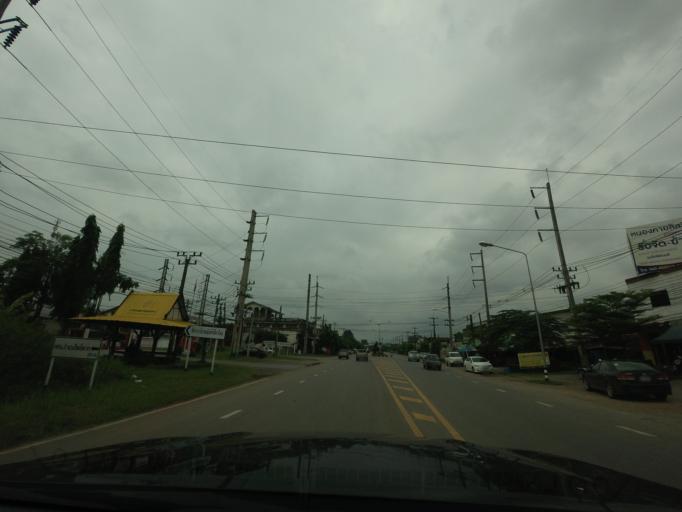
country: TH
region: Nong Khai
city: Si Chiang Mai
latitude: 17.9564
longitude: 102.5925
